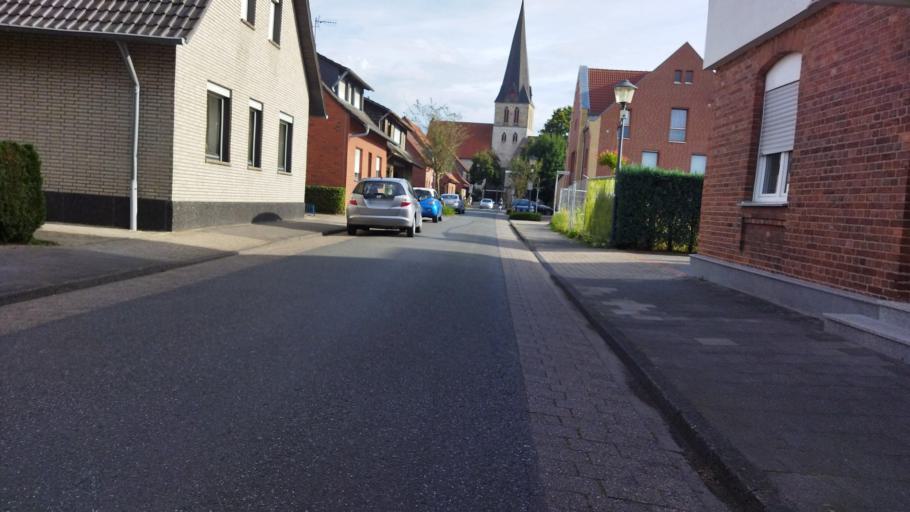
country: DE
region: North Rhine-Westphalia
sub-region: Regierungsbezirk Munster
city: Ostbevern
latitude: 52.0377
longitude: 7.8387
